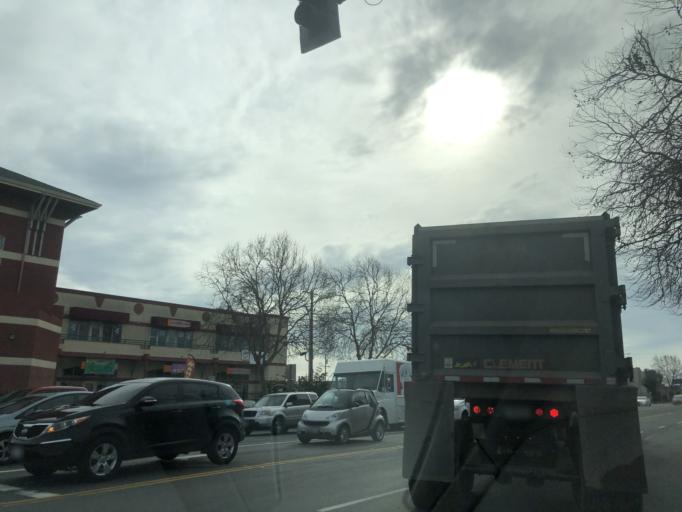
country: US
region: California
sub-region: Alameda County
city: San Leandro
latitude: 37.7392
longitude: -122.1799
